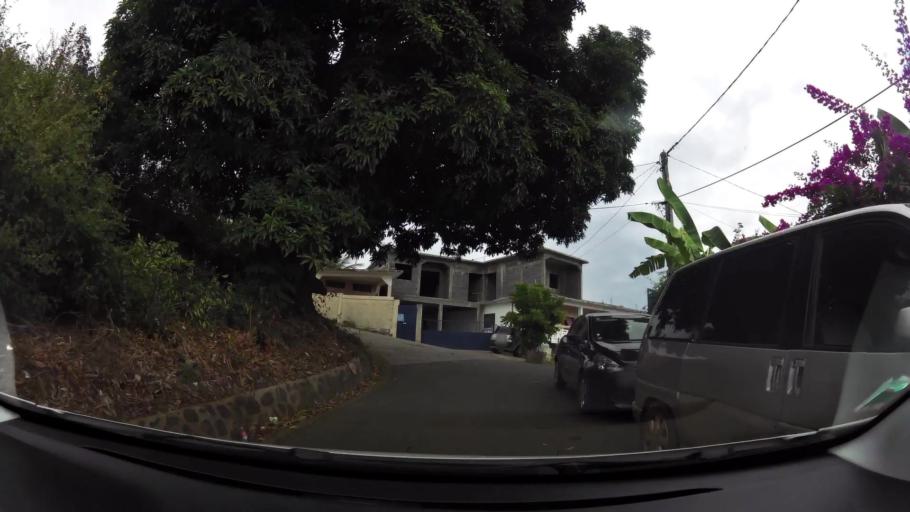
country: YT
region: Sada
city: Sada
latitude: -12.8527
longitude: 45.0953
